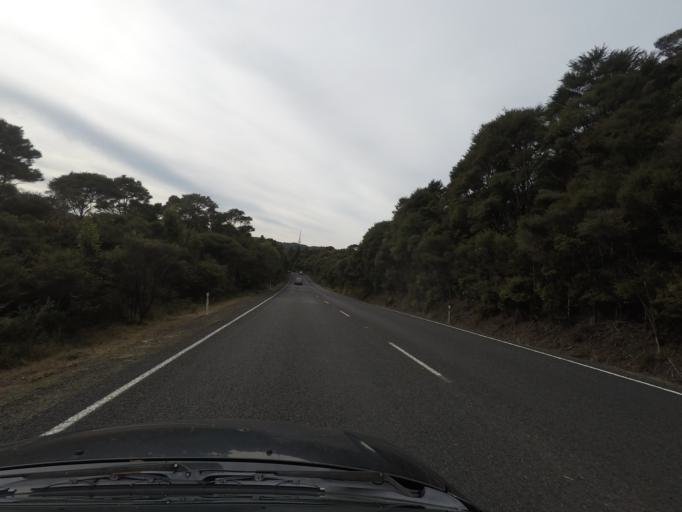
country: NZ
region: Auckland
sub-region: Auckland
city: Titirangi
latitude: -36.9413
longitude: 174.5531
